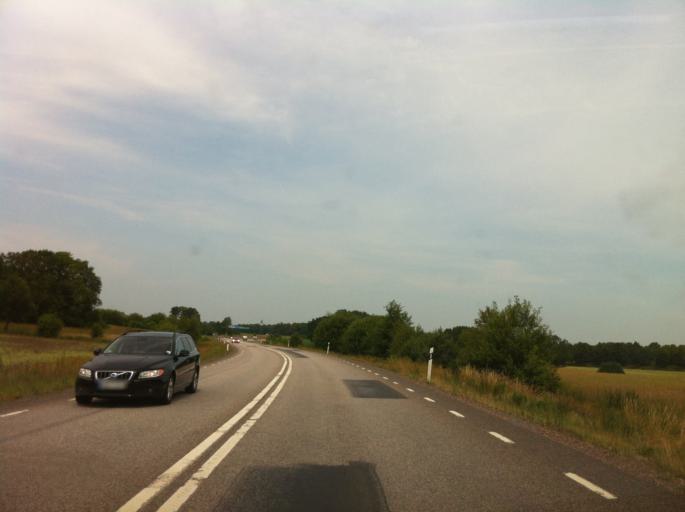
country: SE
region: Kalmar
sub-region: Torsas Kommun
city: Torsas
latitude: 56.4308
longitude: 16.0778
